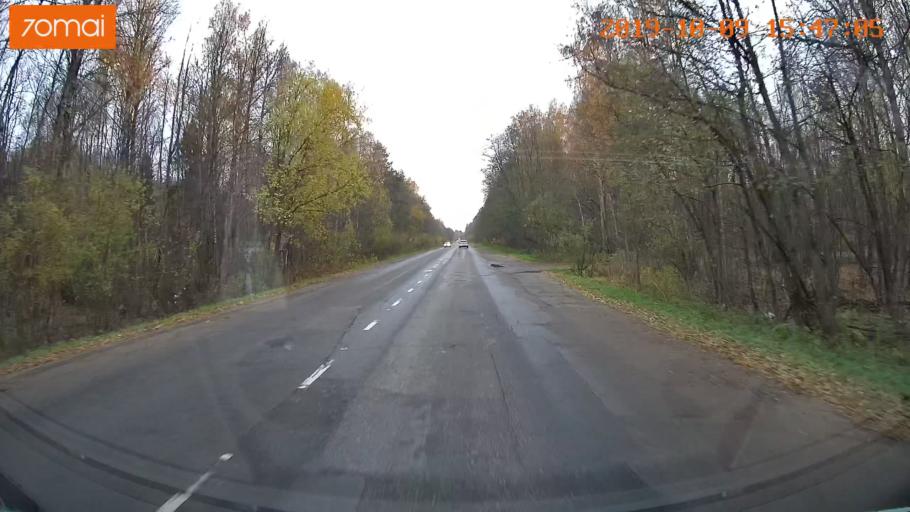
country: RU
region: Kostroma
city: Oktyabr'skiy
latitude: 57.8200
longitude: 41.0340
